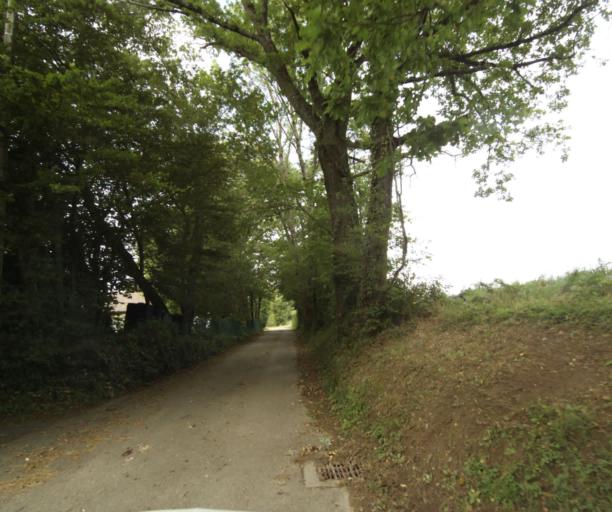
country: FR
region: Rhone-Alpes
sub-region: Departement de la Haute-Savoie
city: Margencel
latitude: 46.3436
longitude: 6.4332
